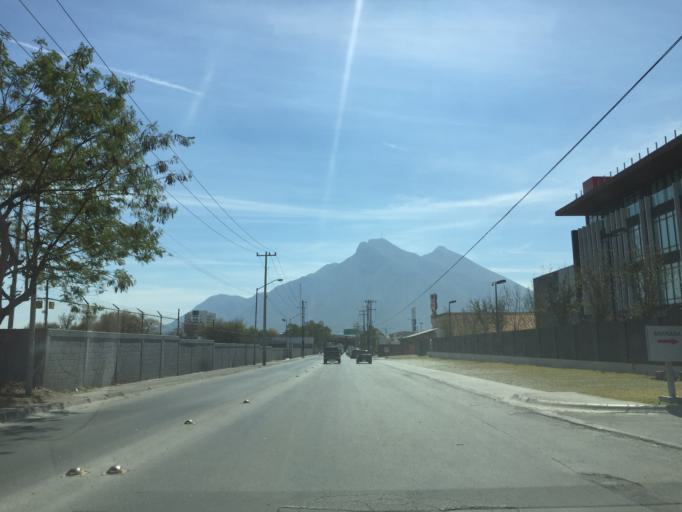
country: MX
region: Nuevo Leon
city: Guadalupe
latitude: 25.6964
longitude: -100.2397
